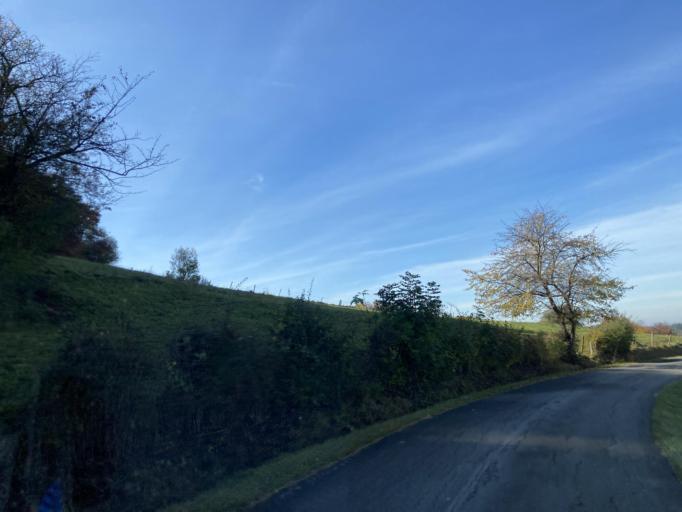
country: DE
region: Baden-Wuerttemberg
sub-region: Tuebingen Region
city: Gomaringen
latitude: 48.4097
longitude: 9.1194
